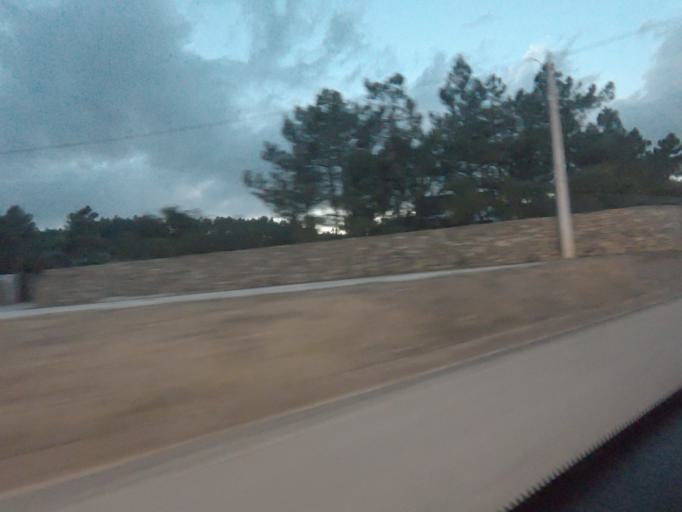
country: PT
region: Viseu
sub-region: Armamar
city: Armamar
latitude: 41.1055
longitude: -7.7062
